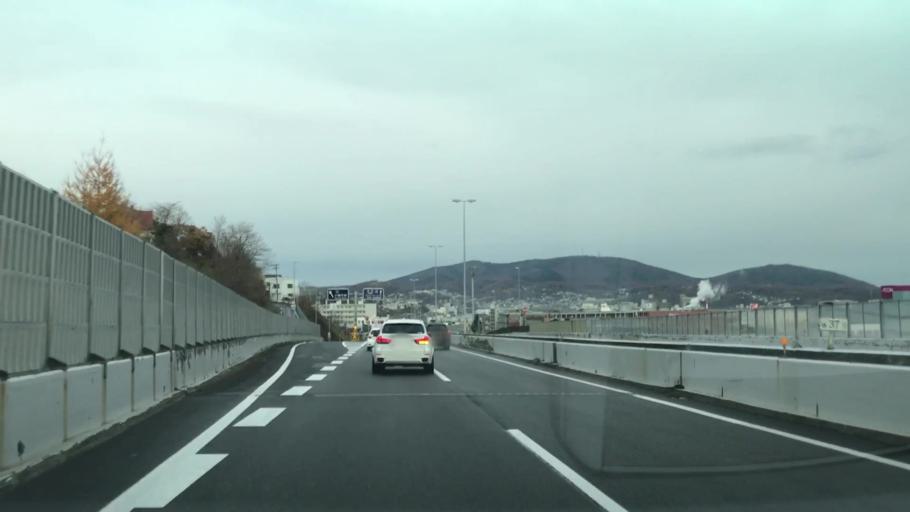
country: JP
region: Hokkaido
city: Otaru
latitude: 43.1791
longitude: 141.0226
